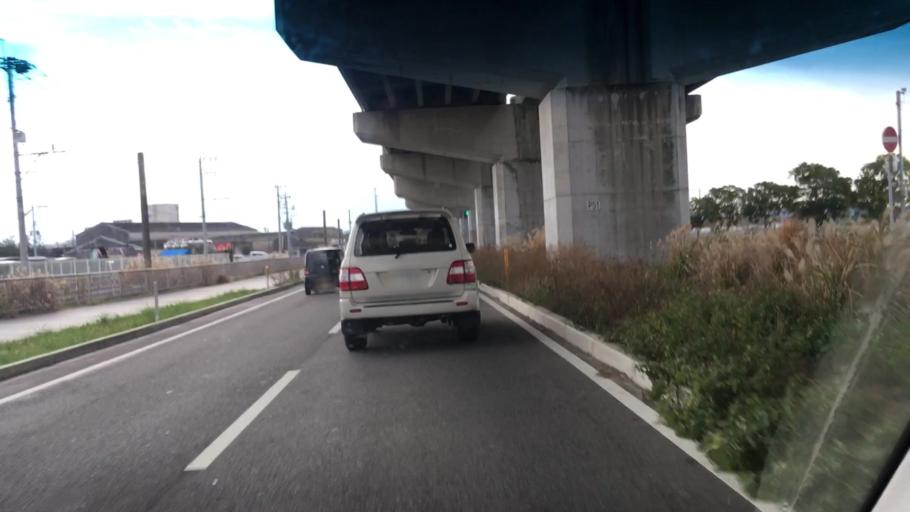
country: JP
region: Fukuoka
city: Maebaru-chuo
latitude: 33.5566
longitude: 130.2277
